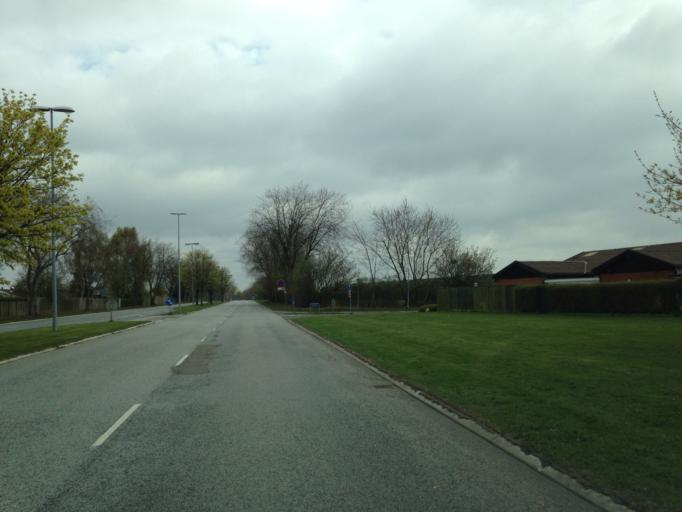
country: DK
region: Capital Region
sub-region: Ishoj Kommune
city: Ishoj
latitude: 55.6123
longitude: 12.3365
